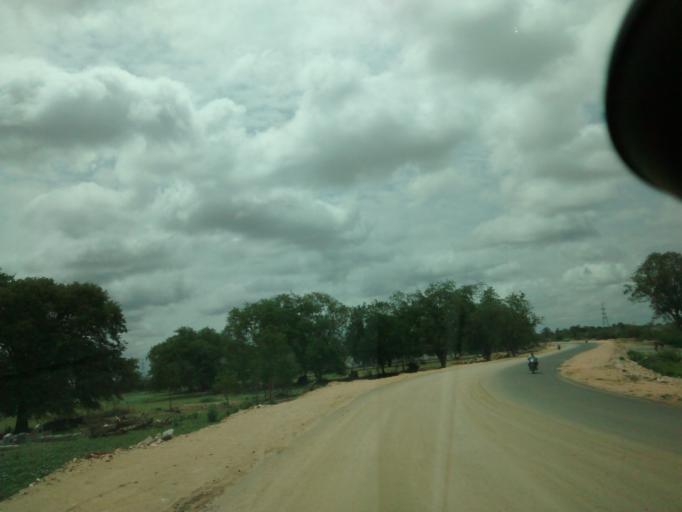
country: IN
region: Andhra Pradesh
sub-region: Anantapur
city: Hindupur
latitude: 13.8114
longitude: 77.5862
